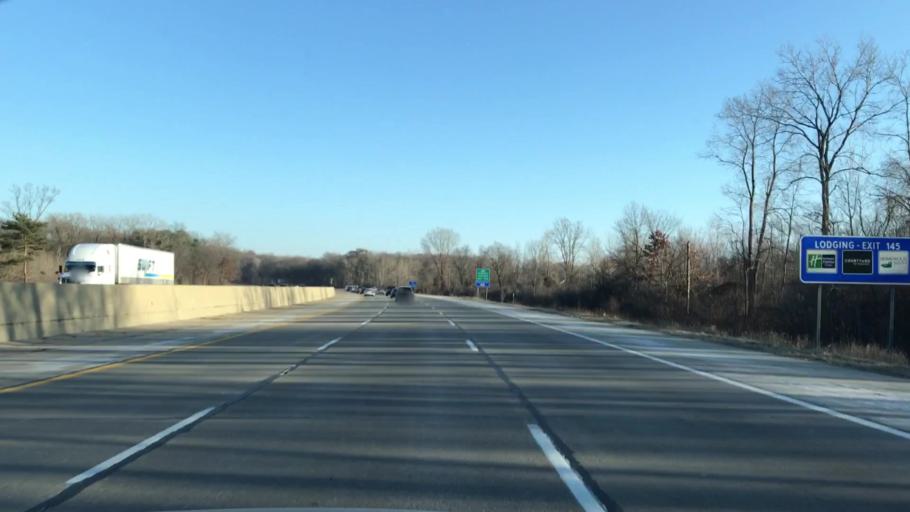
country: US
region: Michigan
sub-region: Livingston County
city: Brighton
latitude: 42.5529
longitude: -83.8141
